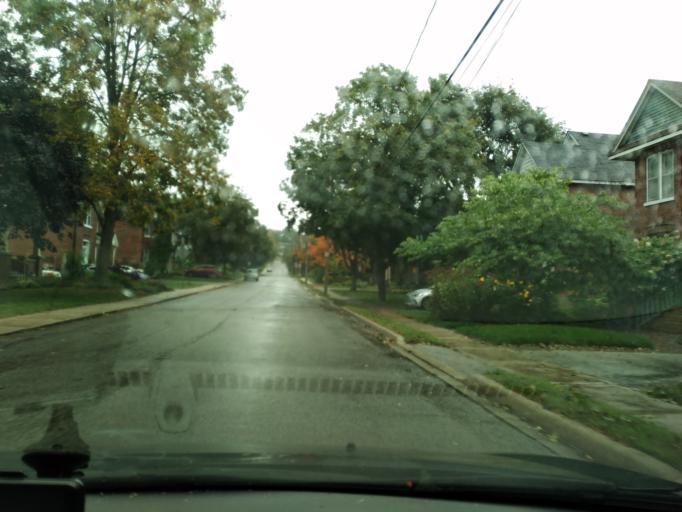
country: CA
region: Ontario
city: Barrie
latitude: 44.3710
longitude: -79.6893
